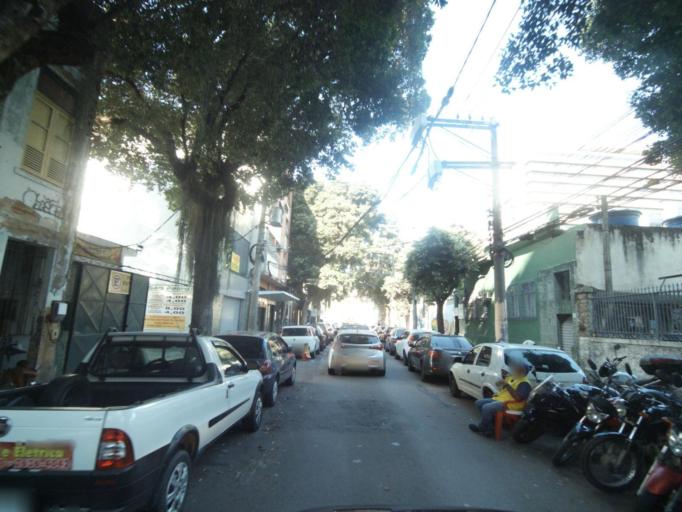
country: BR
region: Rio de Janeiro
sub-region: Niteroi
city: Niteroi
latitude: -22.8918
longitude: -43.1193
